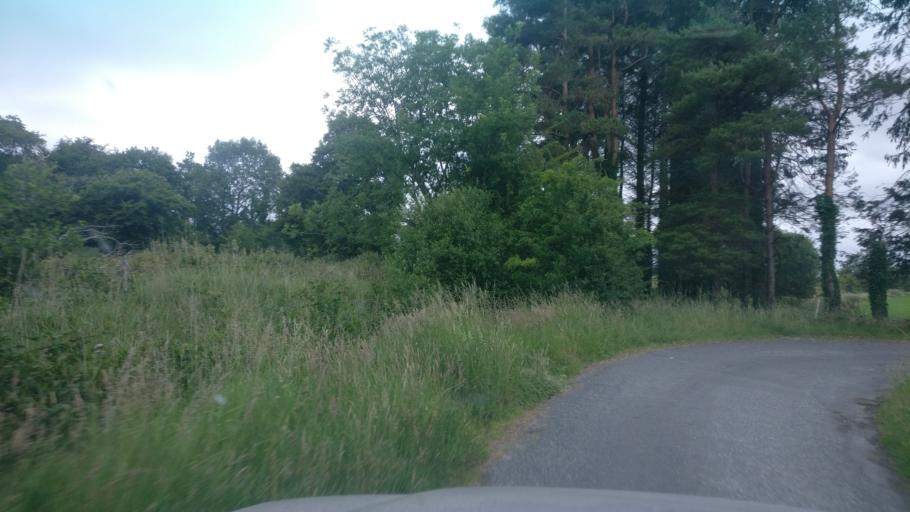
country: IE
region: Connaught
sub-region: County Galway
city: Ballinasloe
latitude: 53.3037
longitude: -8.3489
